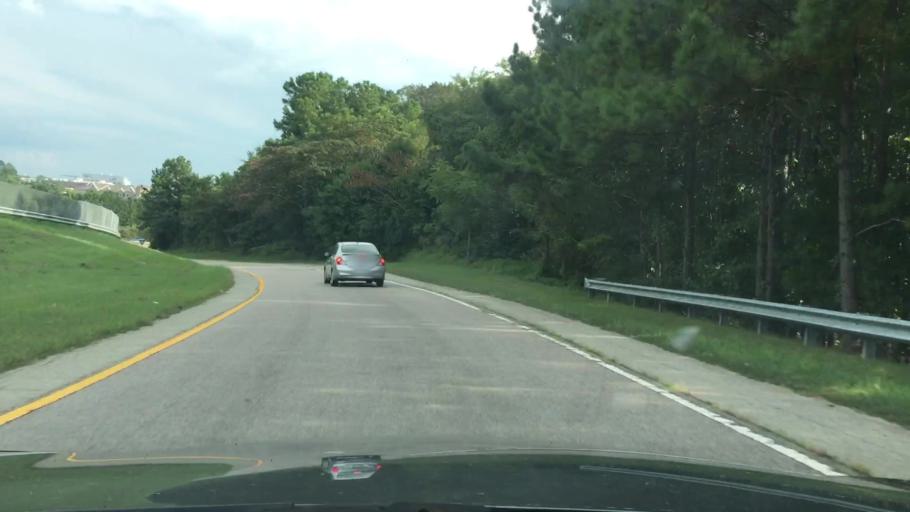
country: US
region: North Carolina
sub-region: Durham County
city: Durham
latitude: 36.0167
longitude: -78.9539
